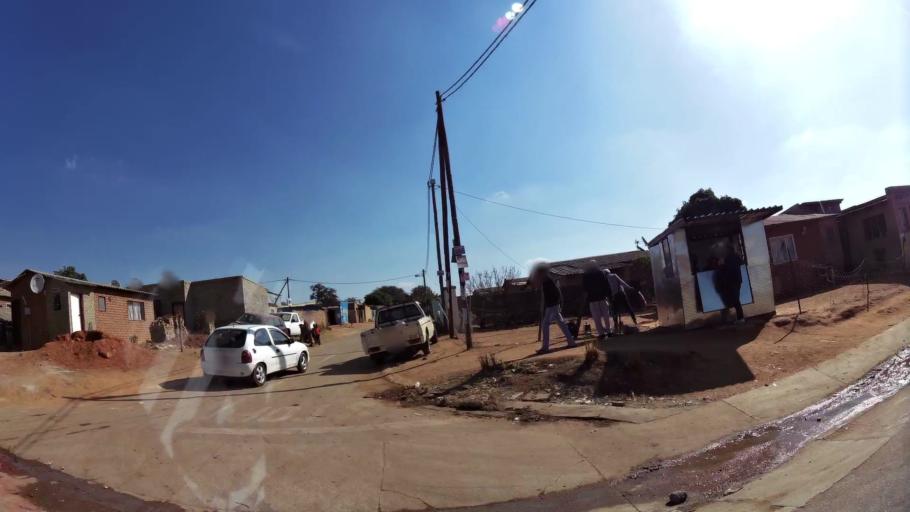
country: ZA
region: Gauteng
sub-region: West Rand District Municipality
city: Muldersdriseloop
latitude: -26.0254
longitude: 27.9281
